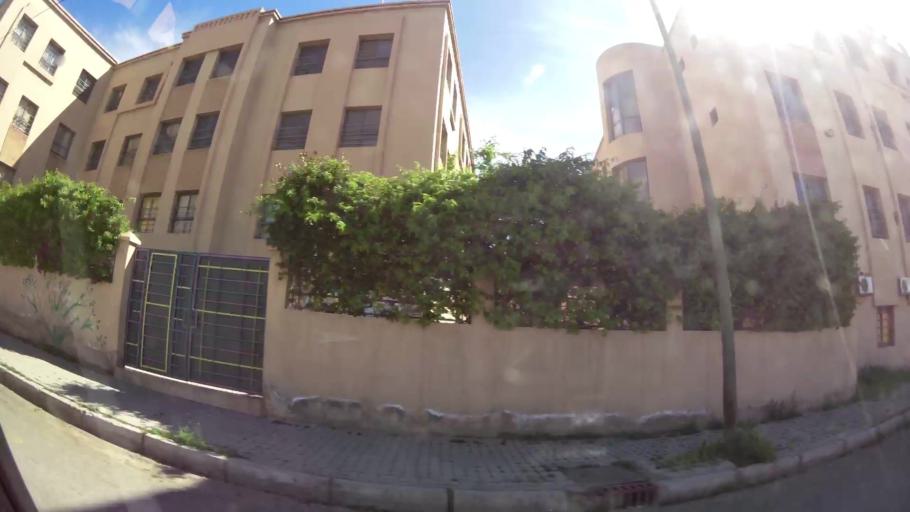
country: MA
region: Marrakech-Tensift-Al Haouz
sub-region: Marrakech
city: Marrakesh
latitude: 31.6791
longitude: -8.0263
